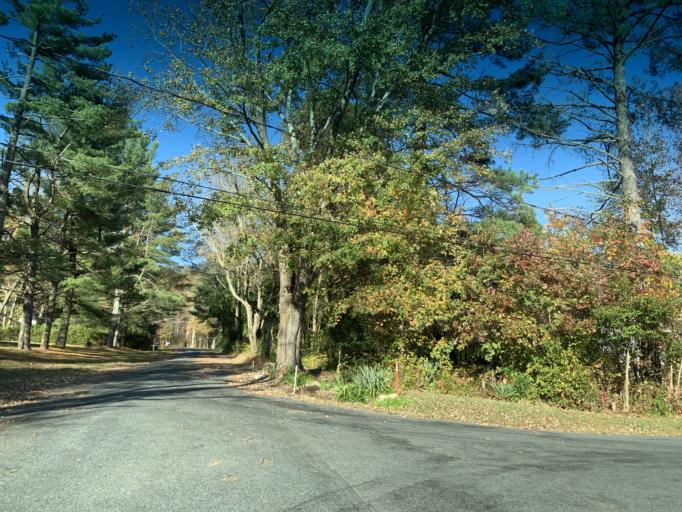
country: US
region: Maryland
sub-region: Harford County
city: Joppatowne
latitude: 39.4466
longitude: -76.3393
